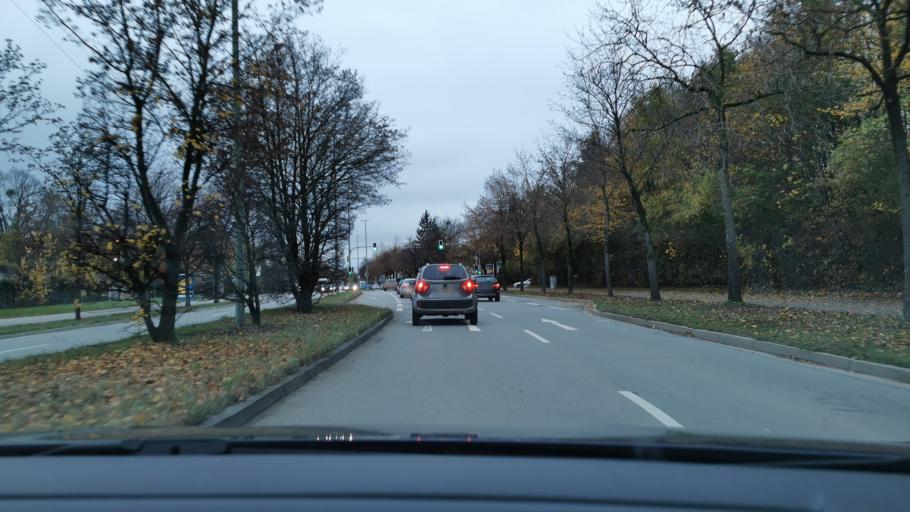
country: DE
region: Bavaria
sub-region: Upper Bavaria
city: Unterfoehring
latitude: 48.2018
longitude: 11.5948
